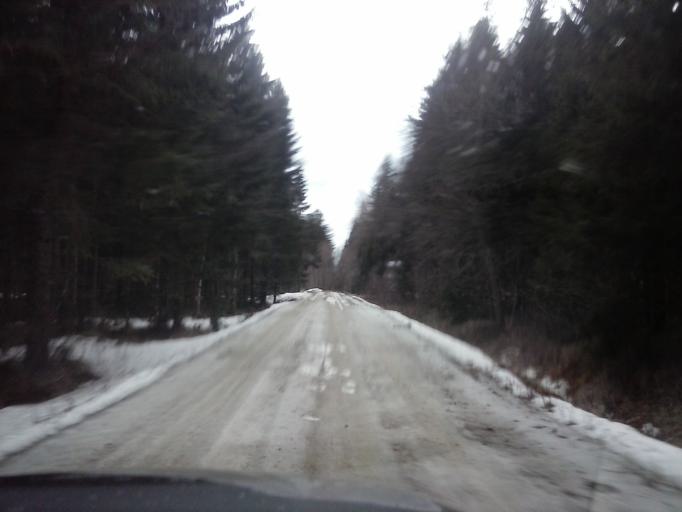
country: EE
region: Ida-Virumaa
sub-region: Johvi vald
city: Johvi
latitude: 59.1814
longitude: 27.3293
